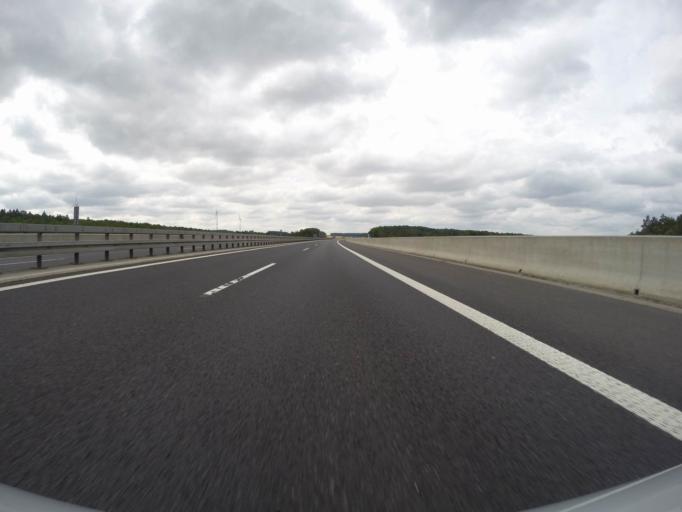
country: DE
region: Bavaria
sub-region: Regierungsbezirk Unterfranken
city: Rannungen
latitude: 50.1969
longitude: 10.2138
